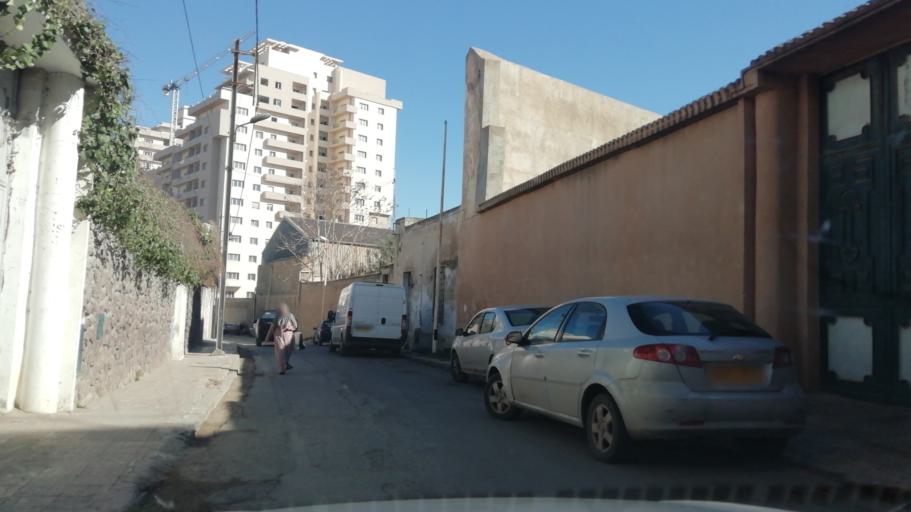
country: DZ
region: Oran
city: Oran
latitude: 35.6996
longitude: -0.6230
